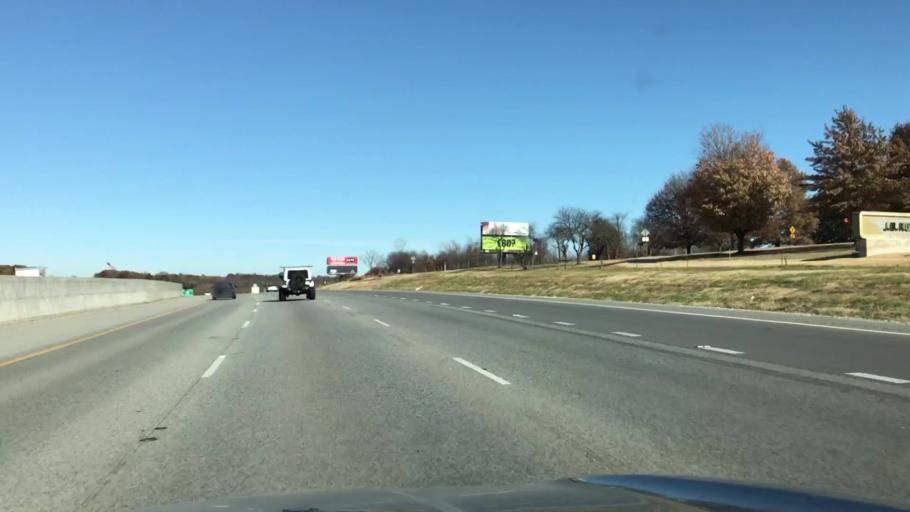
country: US
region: Arkansas
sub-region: Benton County
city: Lowell
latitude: 36.2458
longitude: -94.1510
